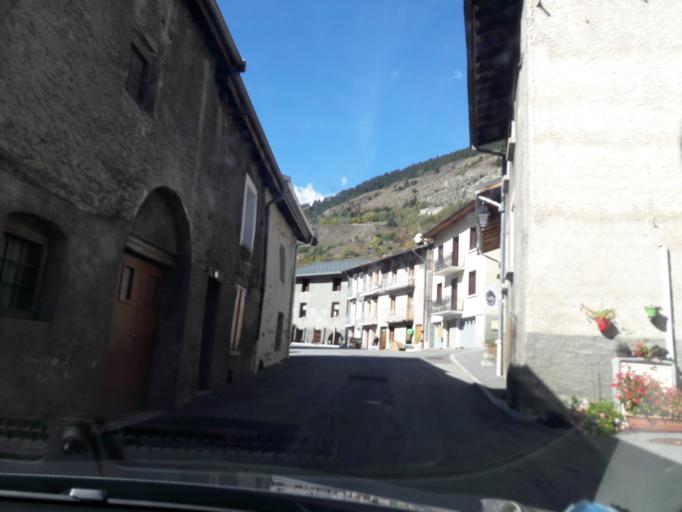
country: FR
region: Rhone-Alpes
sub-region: Departement de la Savoie
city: Modane
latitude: 45.2138
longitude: 6.6977
